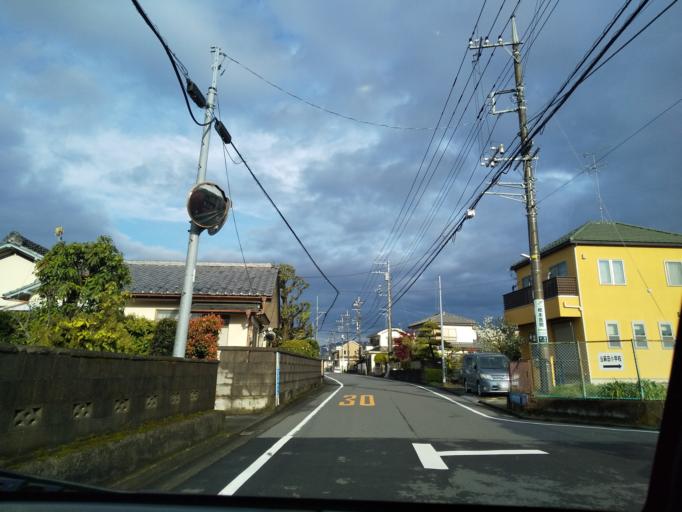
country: JP
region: Tokyo
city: Hachioji
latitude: 35.6021
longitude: 139.3286
